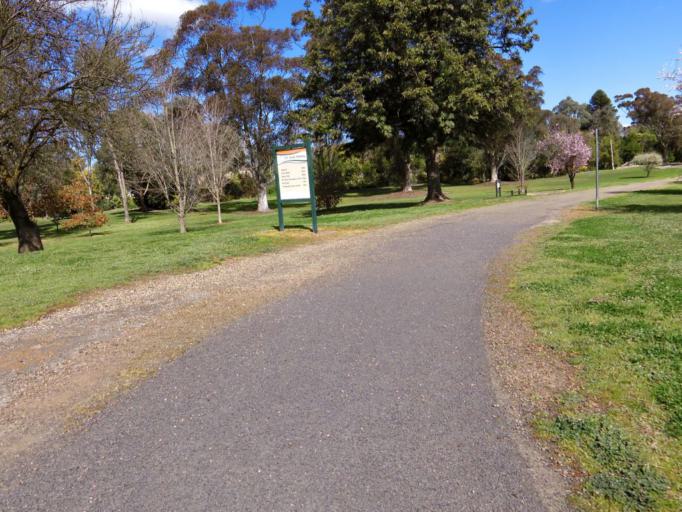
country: AU
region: Victoria
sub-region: Murrindindi
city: Alexandra
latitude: -37.1867
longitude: 145.7151
